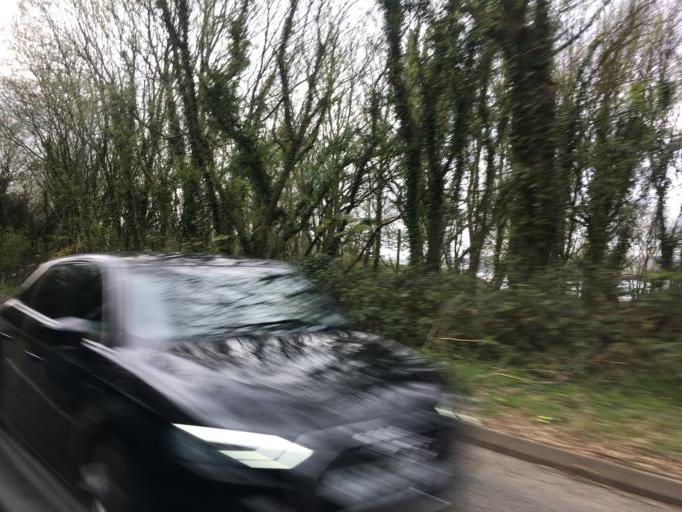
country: GB
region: Wales
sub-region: Gwynedd
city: Y Felinheli
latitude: 53.1731
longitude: -4.2267
